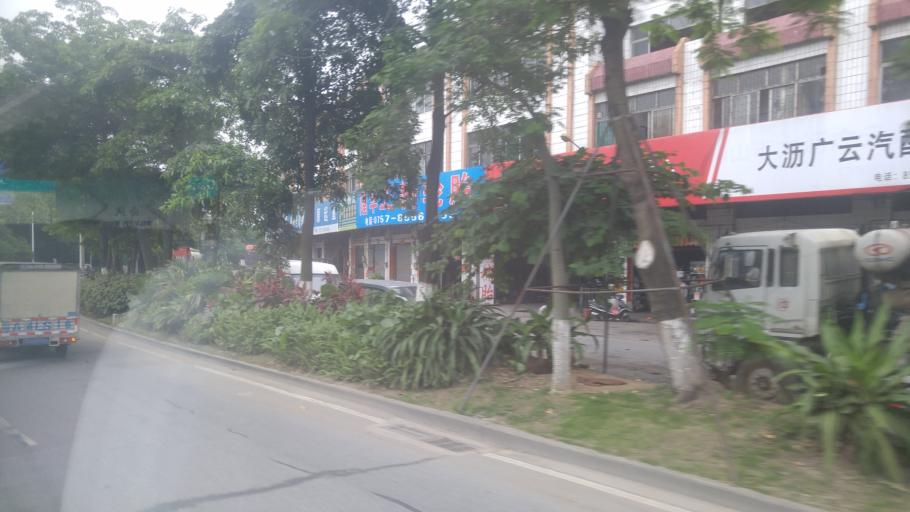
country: CN
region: Guangdong
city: Dali
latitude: 23.1061
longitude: 113.1365
